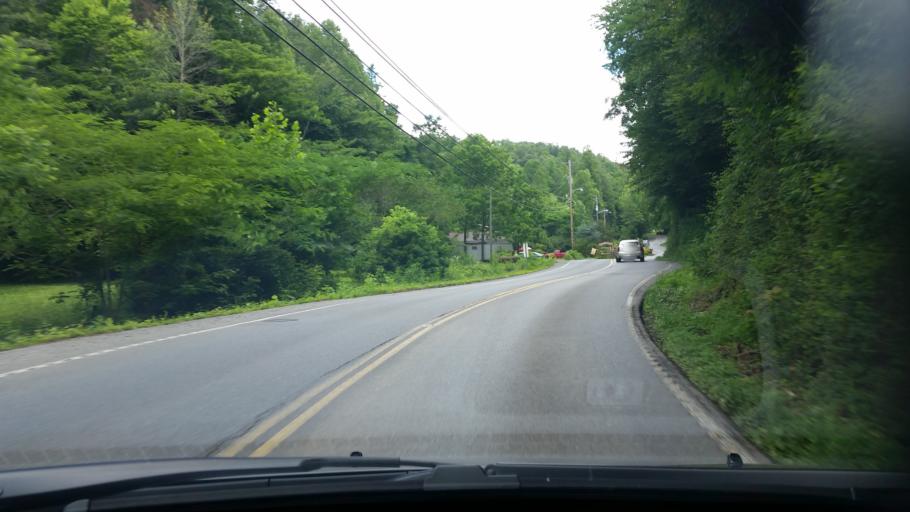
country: US
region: Tennessee
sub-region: Sevier County
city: Gatlinburg
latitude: 35.7352
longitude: -83.4680
